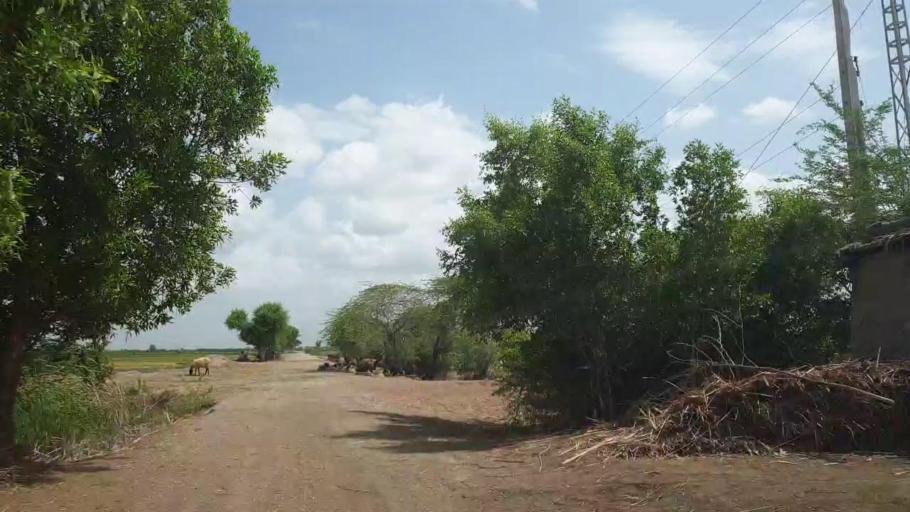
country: PK
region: Sindh
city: Tando Bago
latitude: 24.6499
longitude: 68.9933
